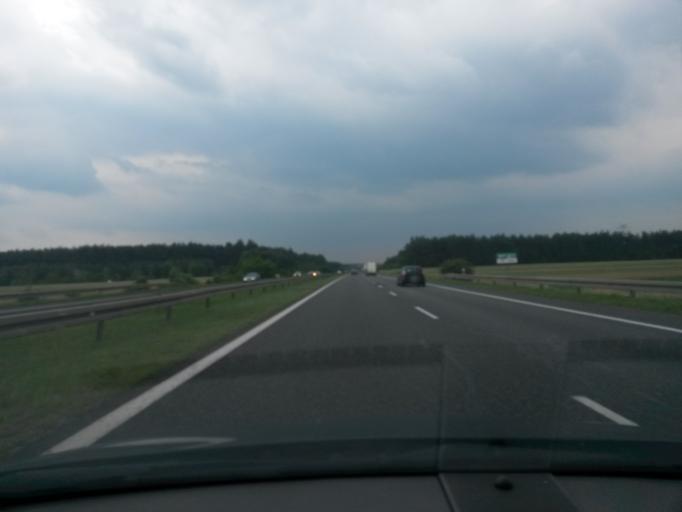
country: PL
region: Lodz Voivodeship
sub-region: Powiat radomszczanski
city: Radomsko
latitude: 51.0650
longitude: 19.3643
